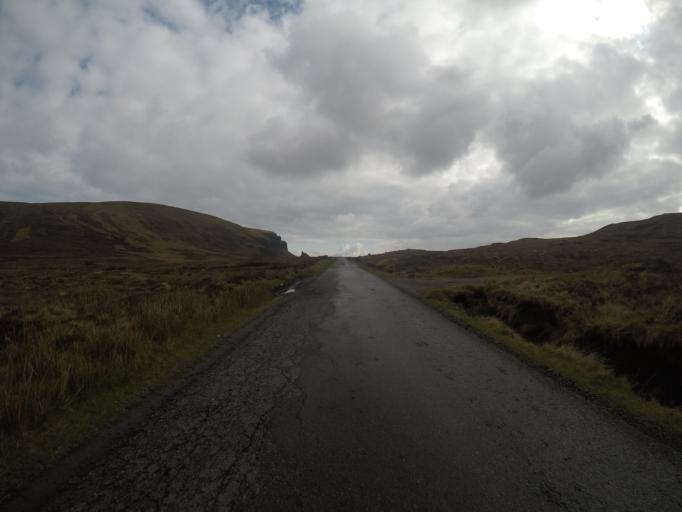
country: GB
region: Scotland
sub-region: Highland
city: Portree
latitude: 57.6251
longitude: -6.2989
